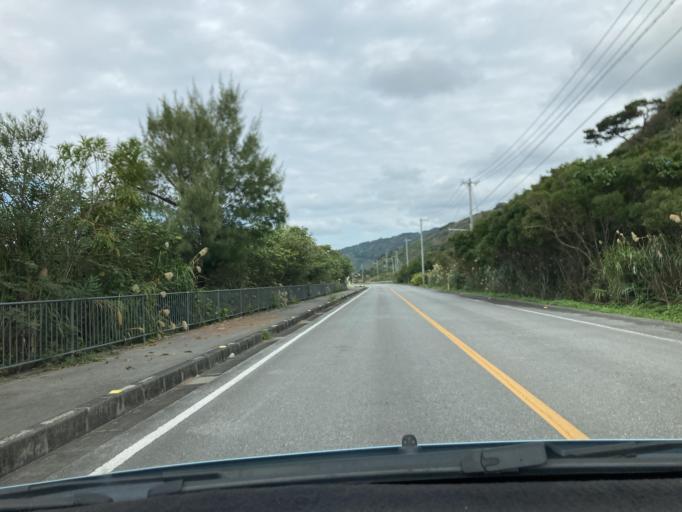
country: JP
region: Okinawa
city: Nago
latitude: 26.7773
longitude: 128.2104
